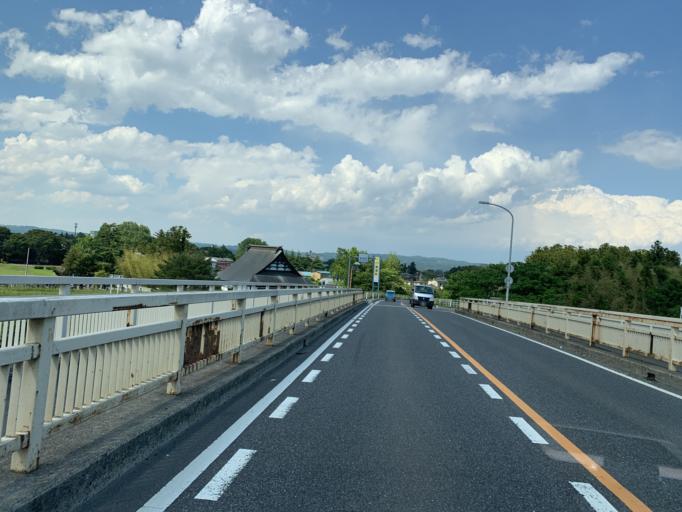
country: JP
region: Miyagi
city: Wakuya
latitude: 38.4984
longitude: 141.1174
